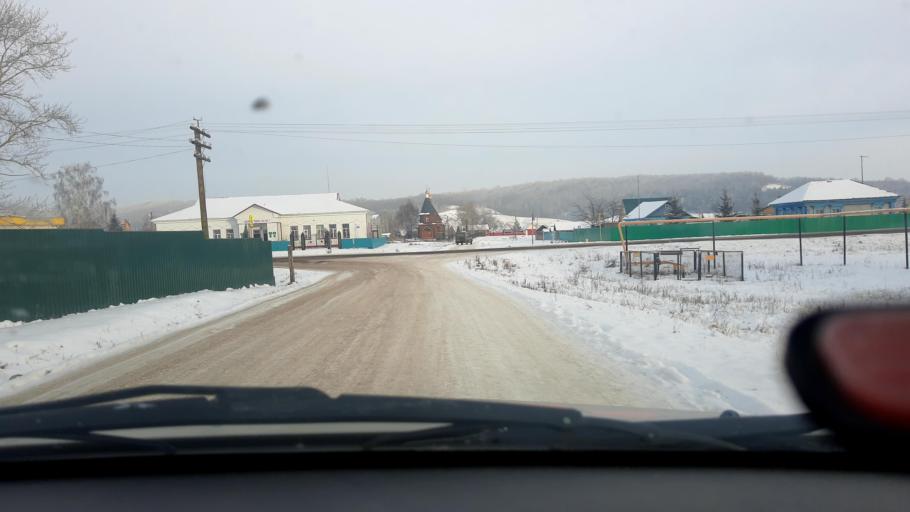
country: RU
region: Bashkortostan
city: Tolbazy
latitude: 54.3563
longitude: 55.8451
